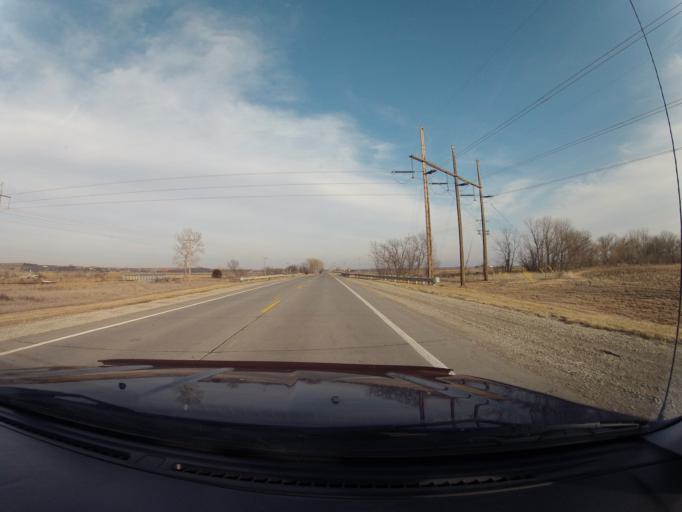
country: US
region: Kansas
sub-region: Pottawatomie County
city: Saint Marys
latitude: 39.2164
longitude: -96.1671
